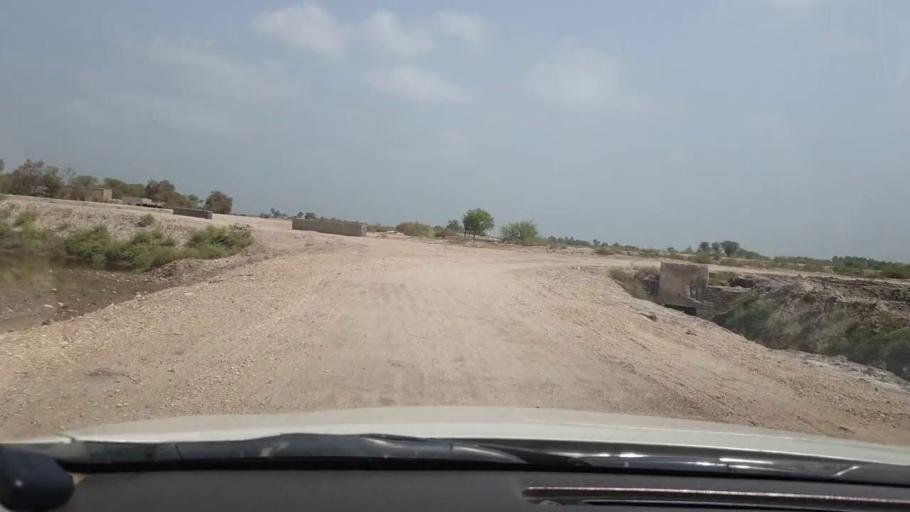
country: PK
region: Sindh
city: Shikarpur
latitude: 28.0116
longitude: 68.5564
